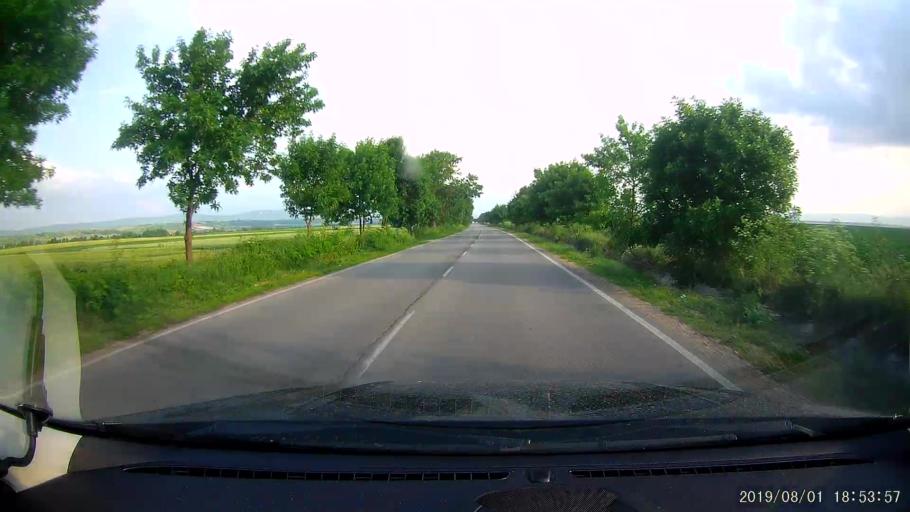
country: BG
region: Shumen
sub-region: Obshtina Shumen
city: Shumen
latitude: 43.2107
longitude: 26.9986
